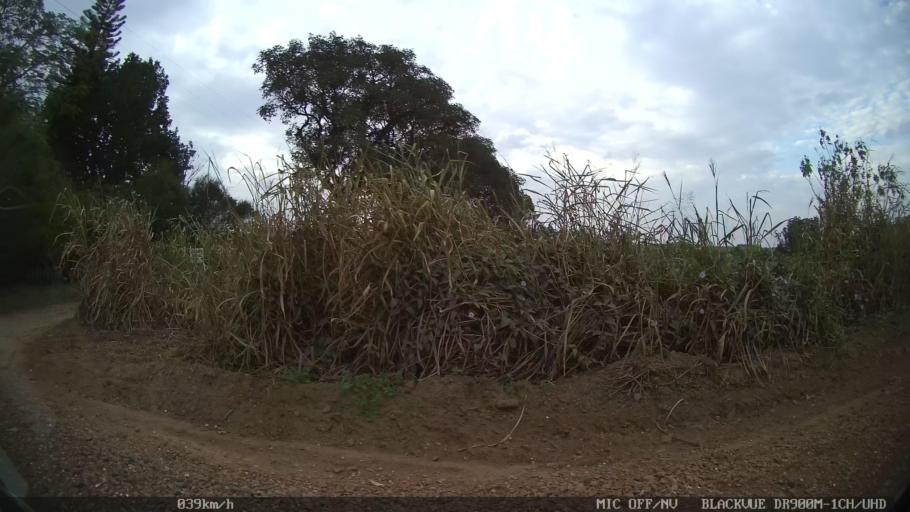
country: BR
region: Sao Paulo
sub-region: Americana
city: Americana
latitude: -22.6566
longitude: -47.3608
